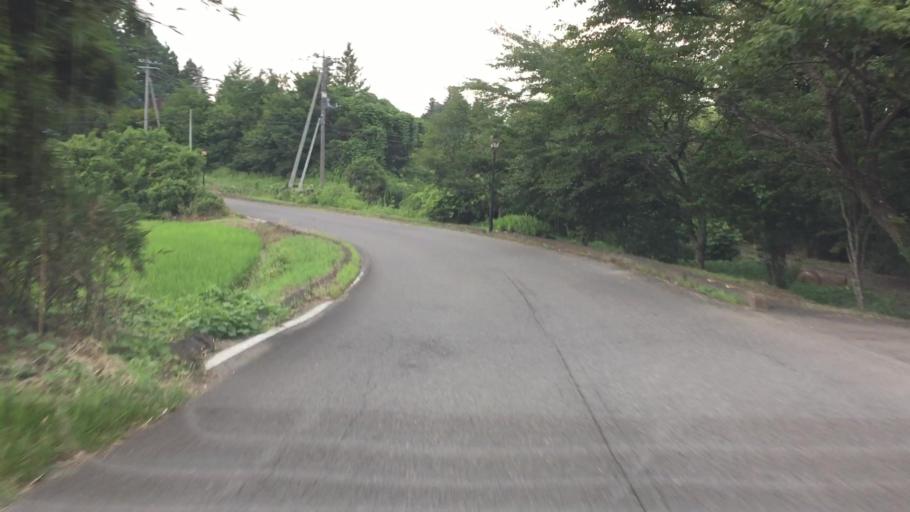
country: JP
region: Tochigi
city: Kuroiso
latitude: 37.0466
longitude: 140.0289
